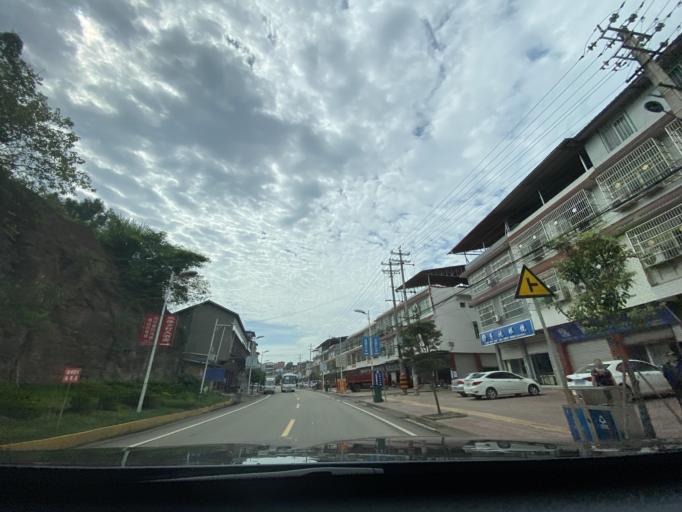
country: CN
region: Sichuan
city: Jiancheng
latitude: 30.4859
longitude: 104.6332
